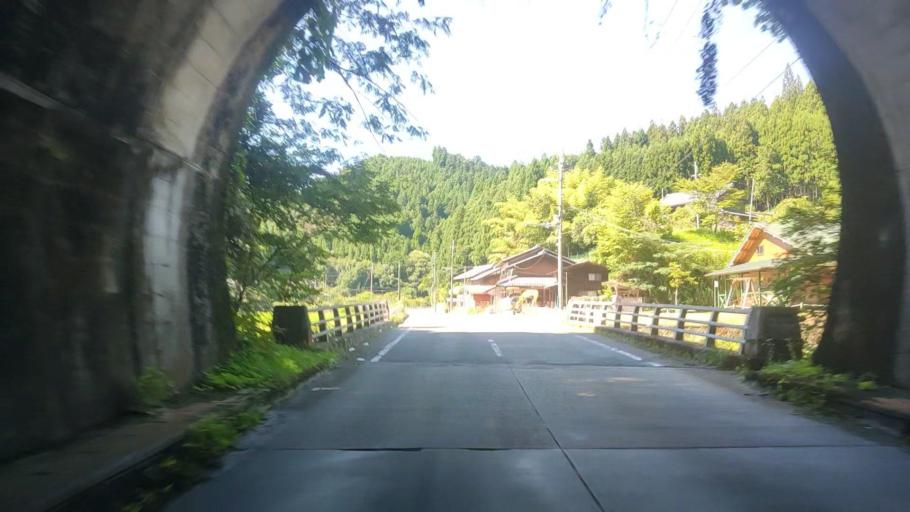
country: JP
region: Nara
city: Yoshino-cho
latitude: 34.4078
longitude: 135.9305
